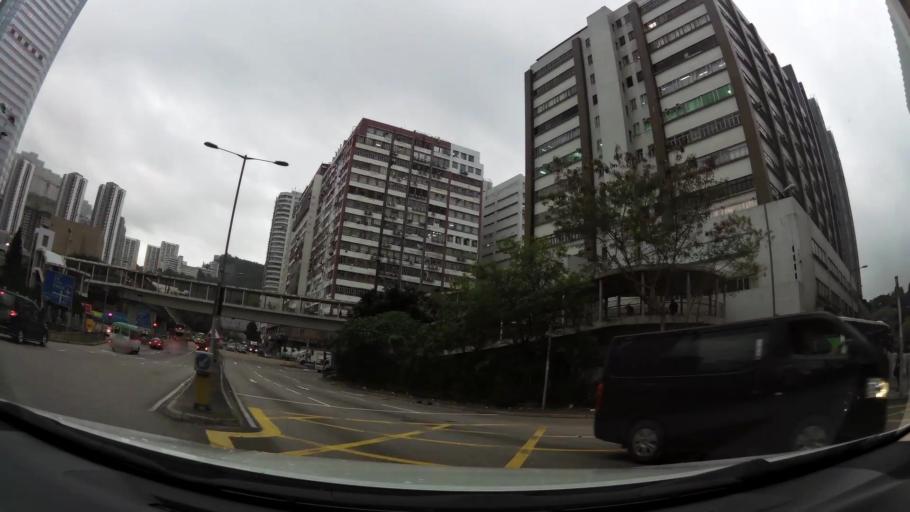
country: HK
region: Tsuen Wan
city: Tsuen Wan
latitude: 22.3579
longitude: 114.1243
